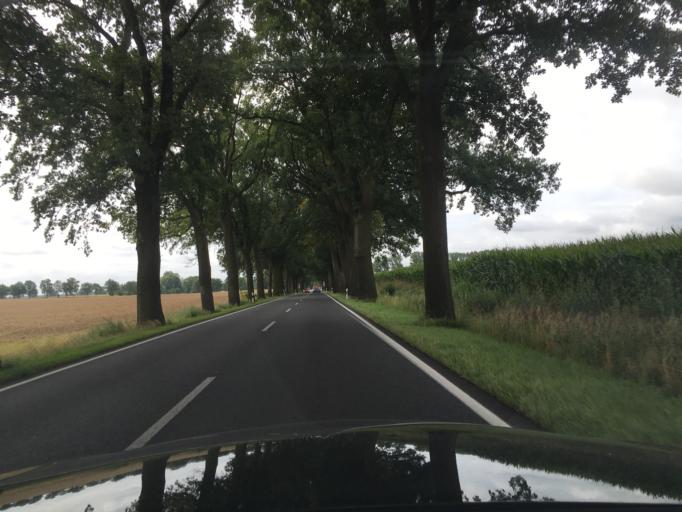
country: DE
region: Brandenburg
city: Gransee
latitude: 52.9432
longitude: 13.1528
